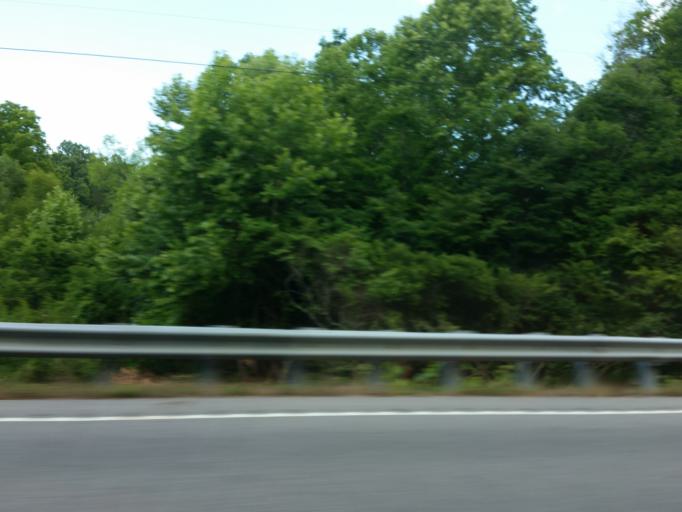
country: US
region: Tennessee
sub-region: Lewis County
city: Hohenwald
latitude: 35.5832
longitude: -87.6767
